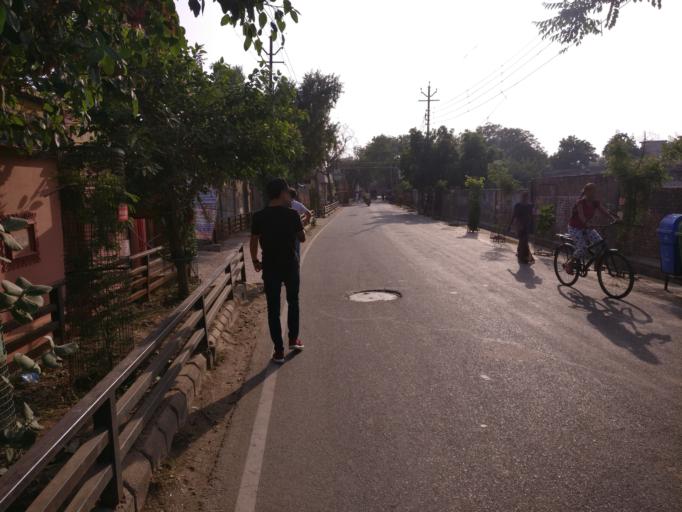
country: IN
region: Uttar Pradesh
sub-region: Mathura
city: Vrindavan
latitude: 27.5682
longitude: 77.6797
